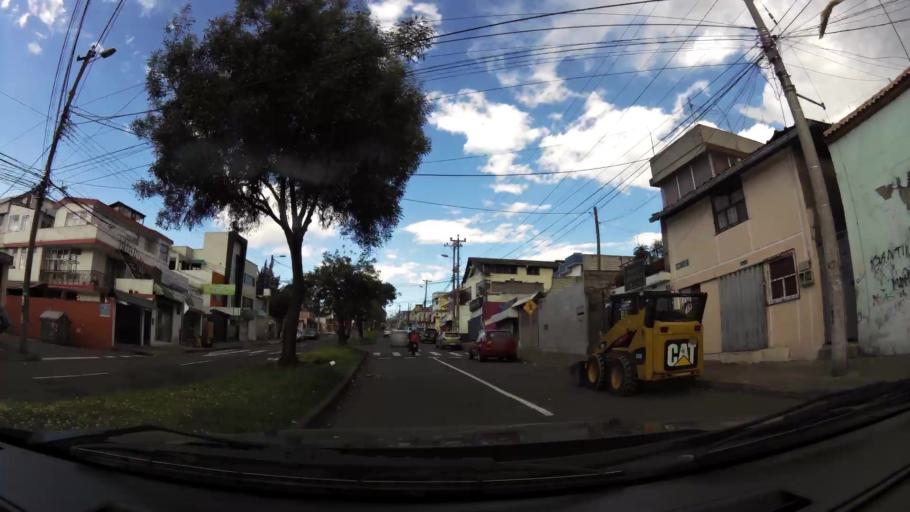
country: EC
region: Pichincha
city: Quito
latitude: -0.1284
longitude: -78.4886
